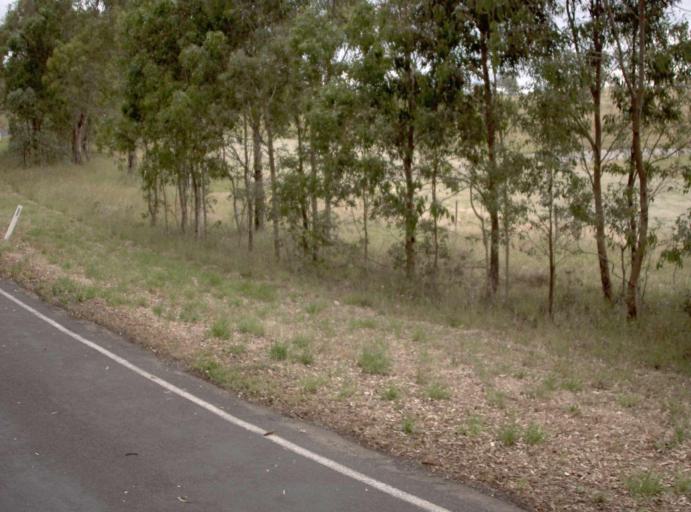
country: AU
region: Victoria
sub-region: East Gippsland
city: Bairnsdale
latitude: -37.7312
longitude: 147.3132
